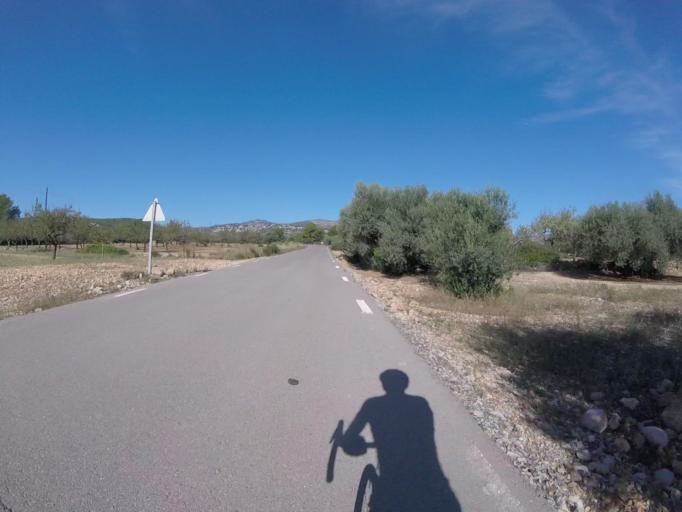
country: ES
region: Valencia
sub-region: Provincia de Castello
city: Sarratella
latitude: 40.2707
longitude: 0.0589
